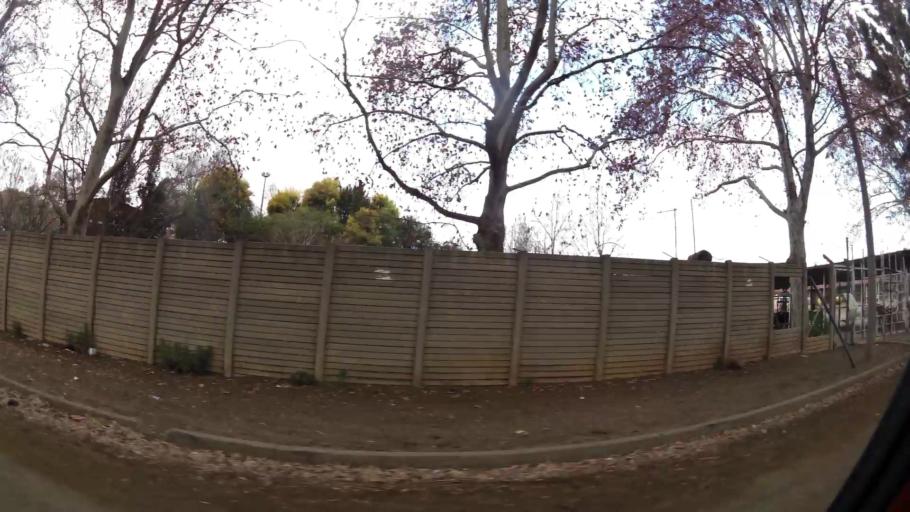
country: ZA
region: Gauteng
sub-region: Sedibeng District Municipality
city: Vanderbijlpark
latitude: -26.6703
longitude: 27.8440
